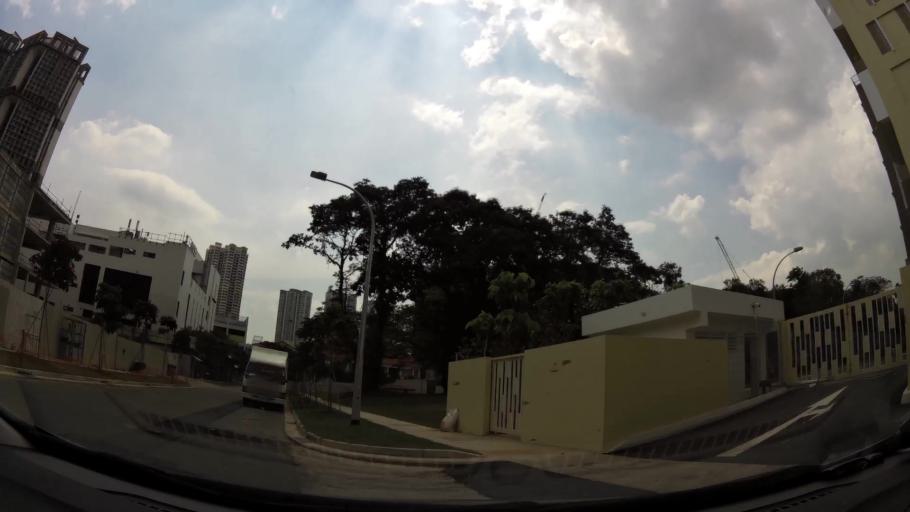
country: SG
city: Singapore
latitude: 1.2979
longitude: 103.8084
